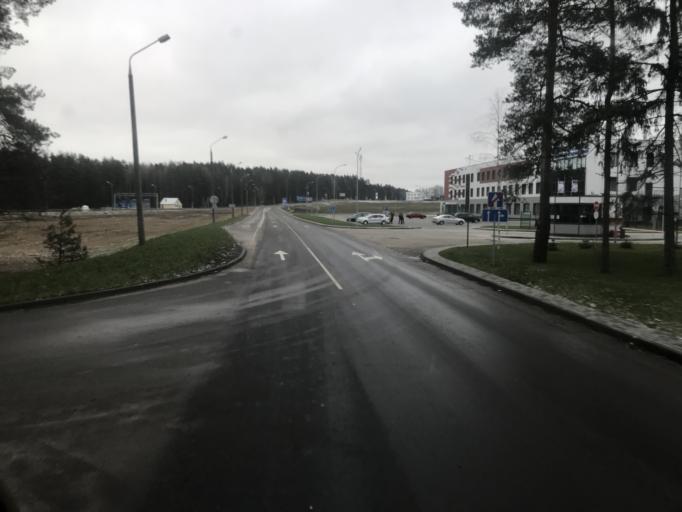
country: BY
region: Grodnenskaya
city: Vyalikaya Byerastavitsa
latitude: 53.1210
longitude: 23.9024
